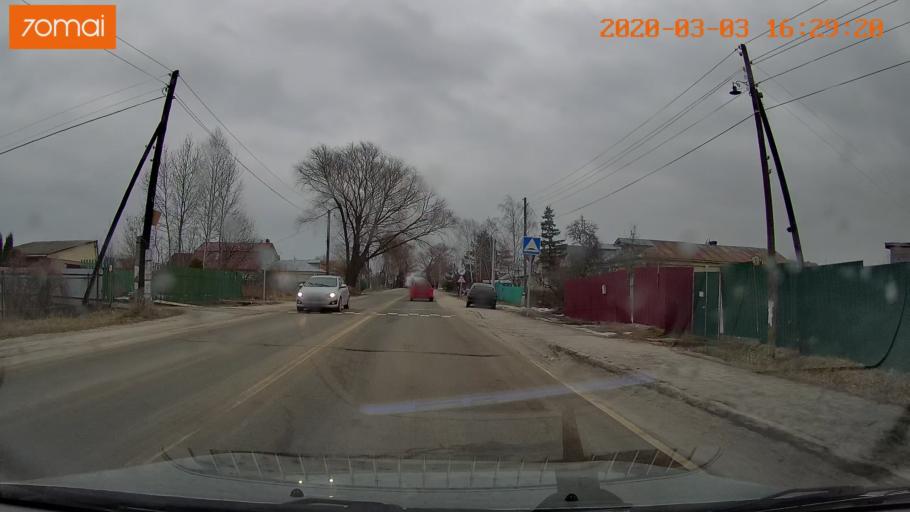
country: RU
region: Moskovskaya
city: Konobeyevo
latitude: 55.4370
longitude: 38.6999
